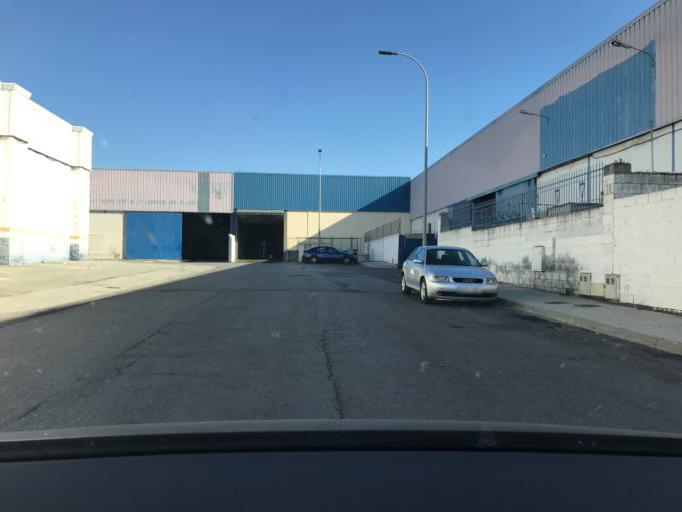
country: ES
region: Andalusia
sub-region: Provincia de Granada
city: Albolote
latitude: 37.2305
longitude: -3.6442
